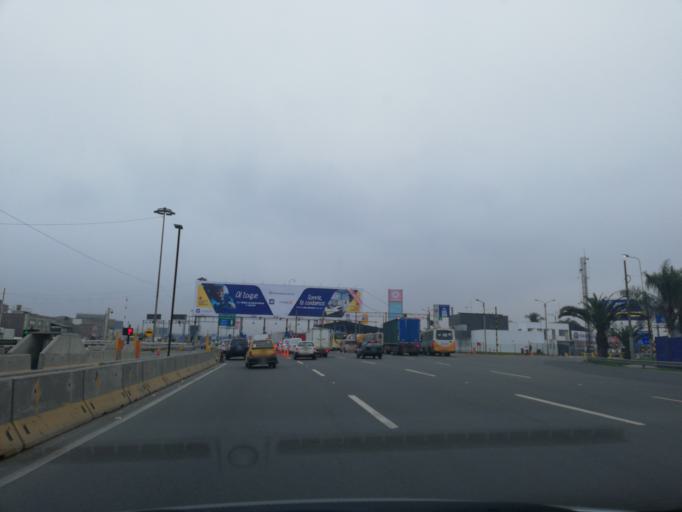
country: PE
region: Lima
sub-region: Lima
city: San Luis
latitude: -12.0680
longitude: -76.9717
